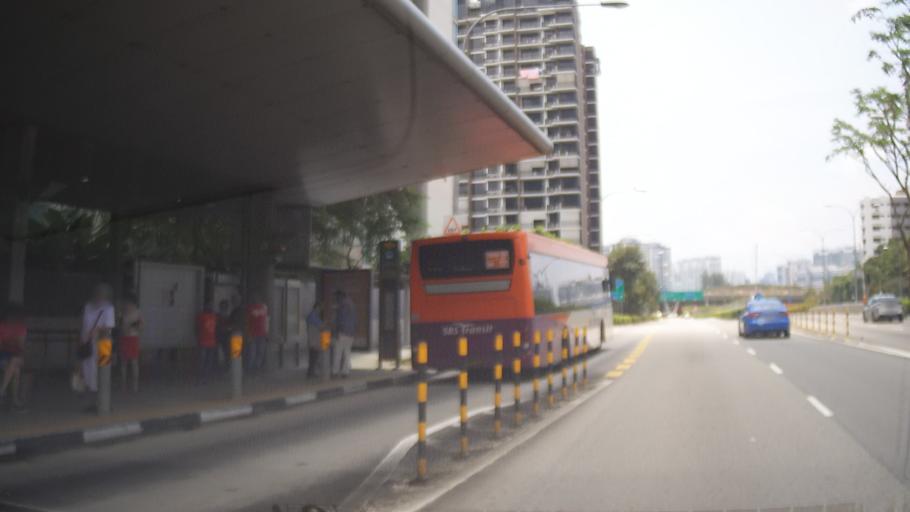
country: SG
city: Singapore
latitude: 1.3311
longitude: 103.8692
